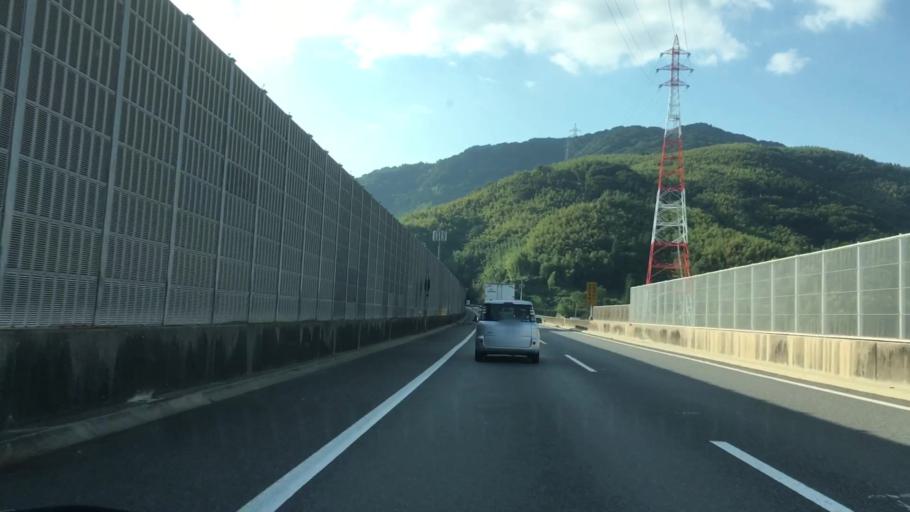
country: JP
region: Yamaguchi
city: Tokuyama
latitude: 34.0867
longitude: 131.7806
